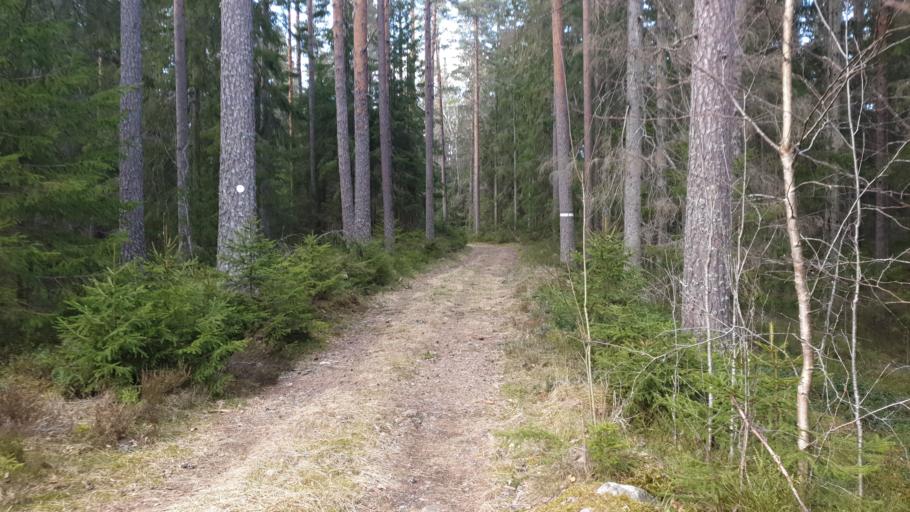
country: SE
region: OErebro
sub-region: Orebro Kommun
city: Garphyttan
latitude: 59.3659
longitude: 14.9766
